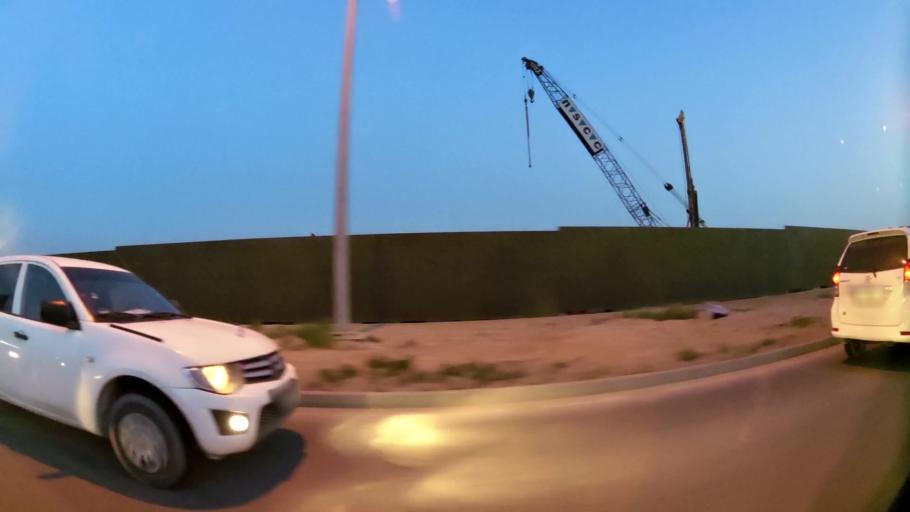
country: QA
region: Baladiyat ar Rayyan
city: Ar Rayyan
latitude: 25.2991
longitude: 51.4472
